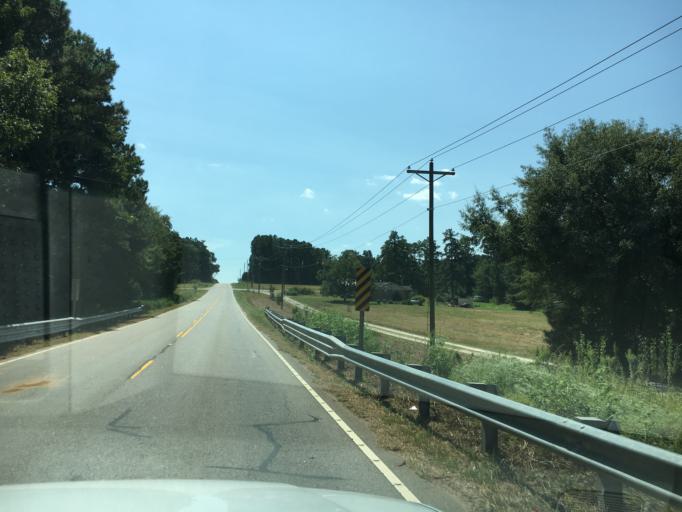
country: US
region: South Carolina
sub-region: Edgefield County
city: Johnston
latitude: 33.9006
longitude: -81.7010
